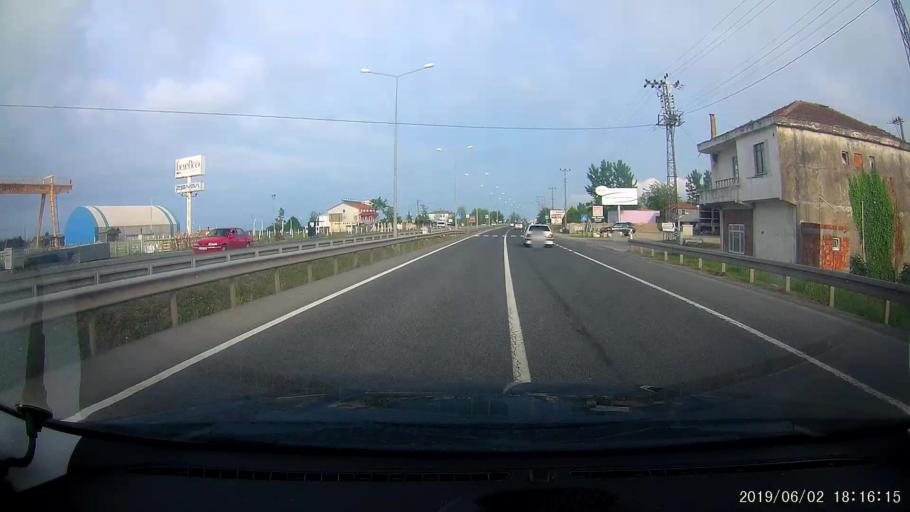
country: TR
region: Ordu
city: Unieh
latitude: 41.1022
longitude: 37.3951
